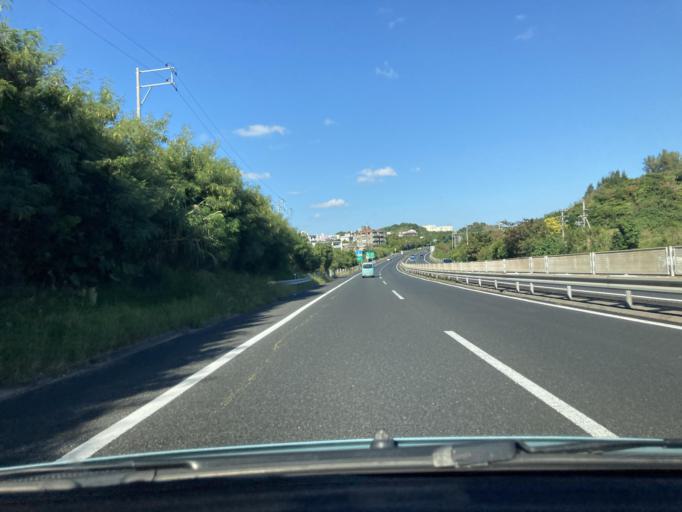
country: JP
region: Okinawa
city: Ginowan
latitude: 26.2421
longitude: 127.7436
